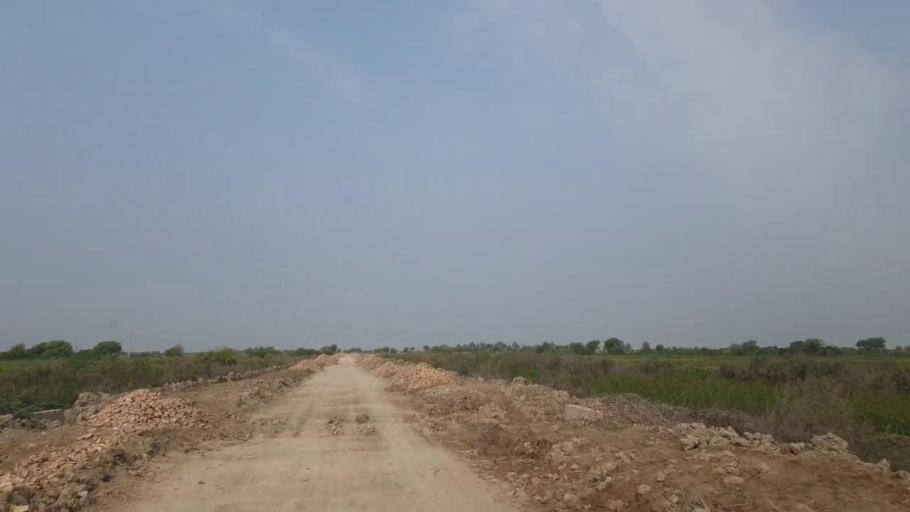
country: PK
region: Sindh
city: Badin
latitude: 24.6084
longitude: 68.7416
